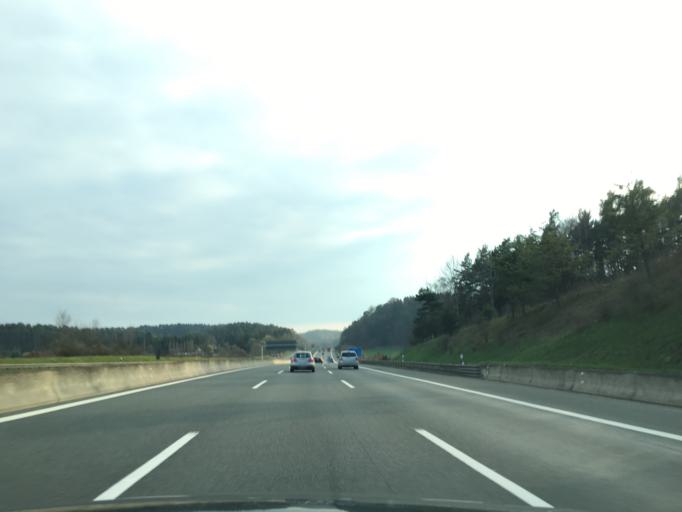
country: DE
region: Bavaria
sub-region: Regierungsbezirk Mittelfranken
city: Velden
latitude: 49.6625
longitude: 11.4656
